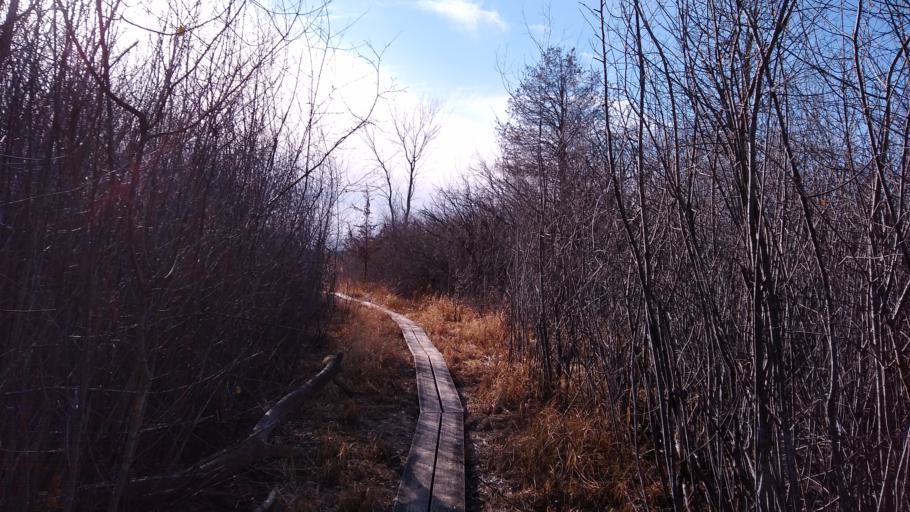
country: US
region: Wisconsin
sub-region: Dane County
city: Madison
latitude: 43.0550
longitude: -89.4054
